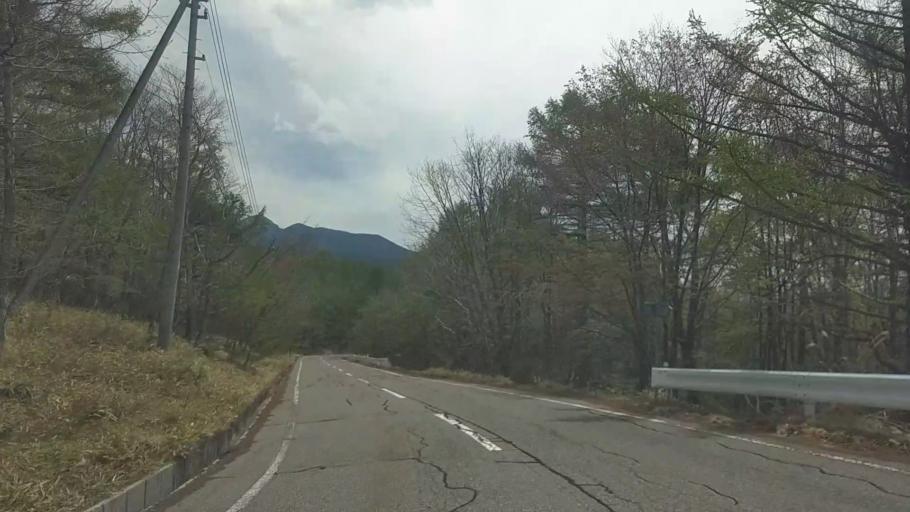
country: JP
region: Nagano
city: Chino
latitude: 36.0510
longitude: 138.3097
